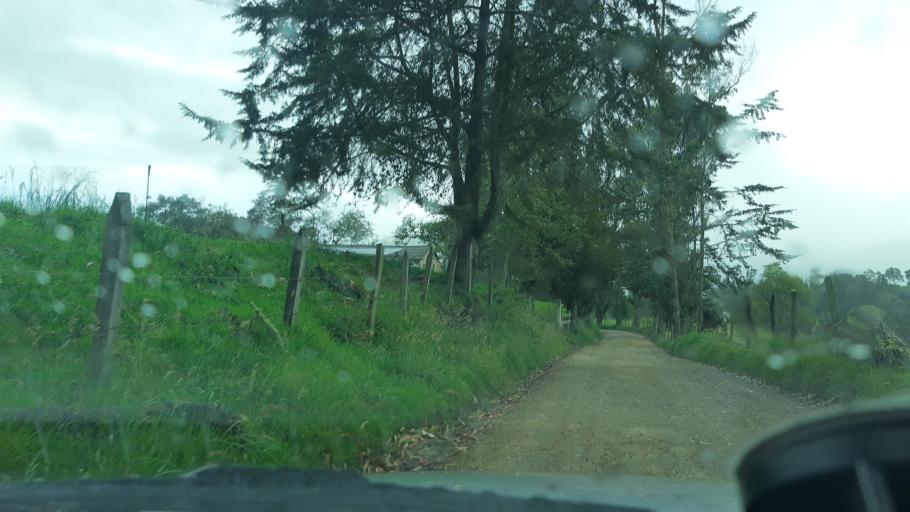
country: CO
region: Cundinamarca
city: Villapinzon
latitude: 5.2233
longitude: -73.5743
